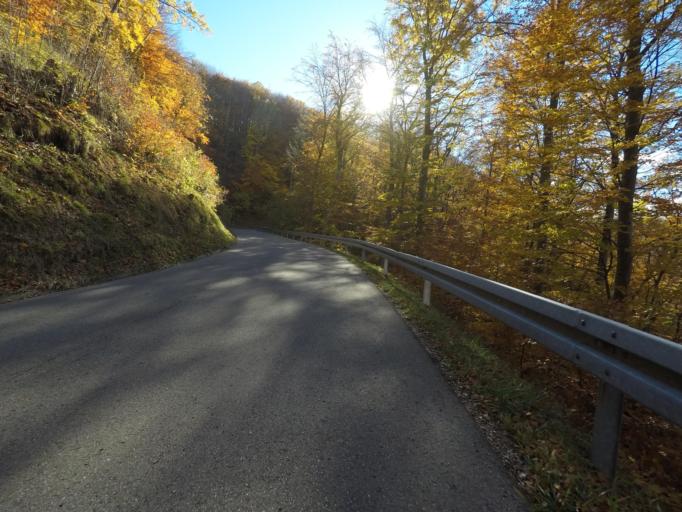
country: DE
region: Baden-Wuerttemberg
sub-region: Tuebingen Region
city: Pfullingen
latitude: 48.4187
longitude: 9.2407
